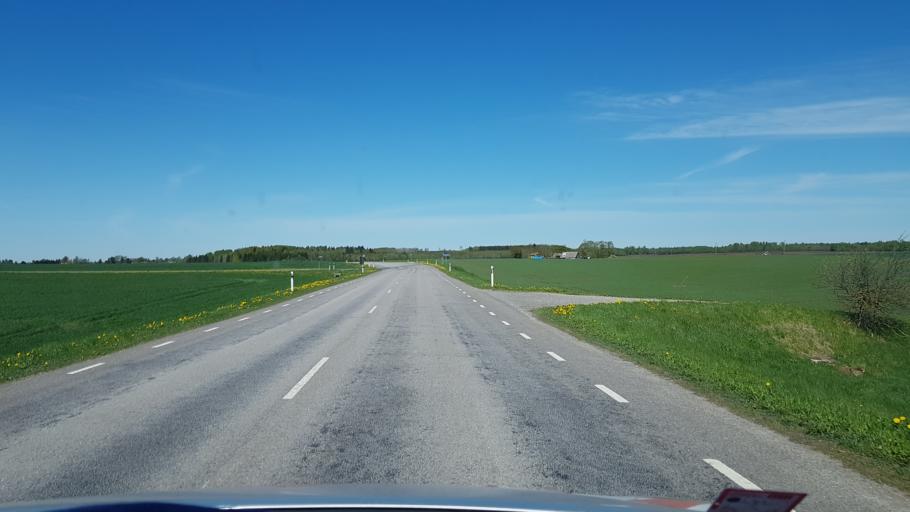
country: EE
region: Tartu
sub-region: Tartu linn
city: Tartu
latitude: 58.3841
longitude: 26.6128
